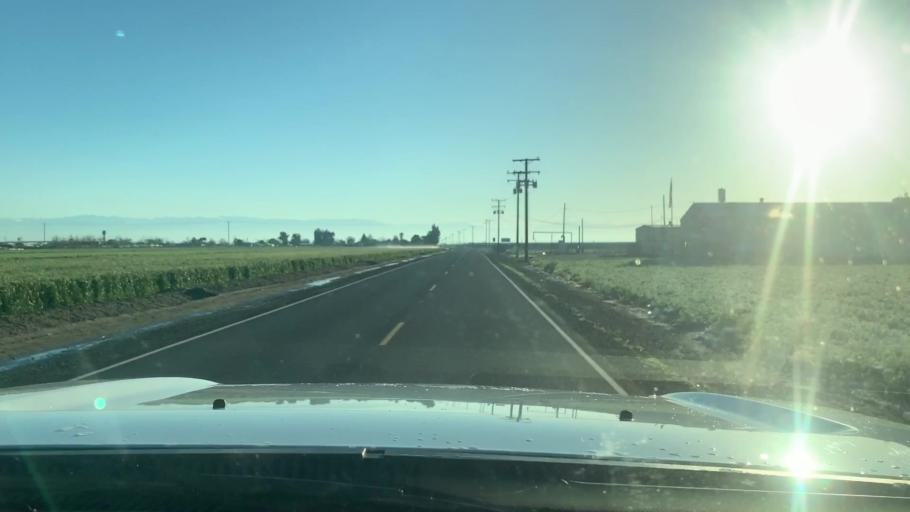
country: US
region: California
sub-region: Tulare County
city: Tulare
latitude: 36.2030
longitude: -119.4790
